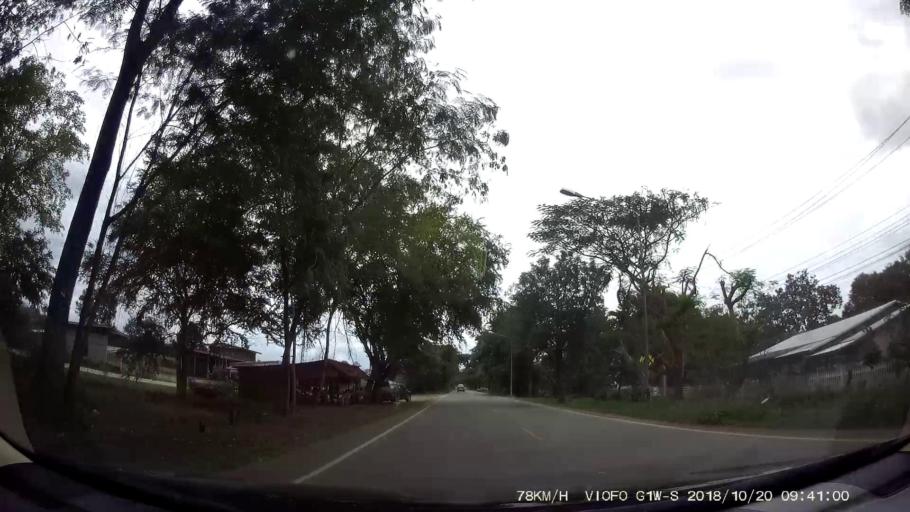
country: TH
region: Chaiyaphum
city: Kaset Sombun
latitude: 16.4487
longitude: 101.9590
